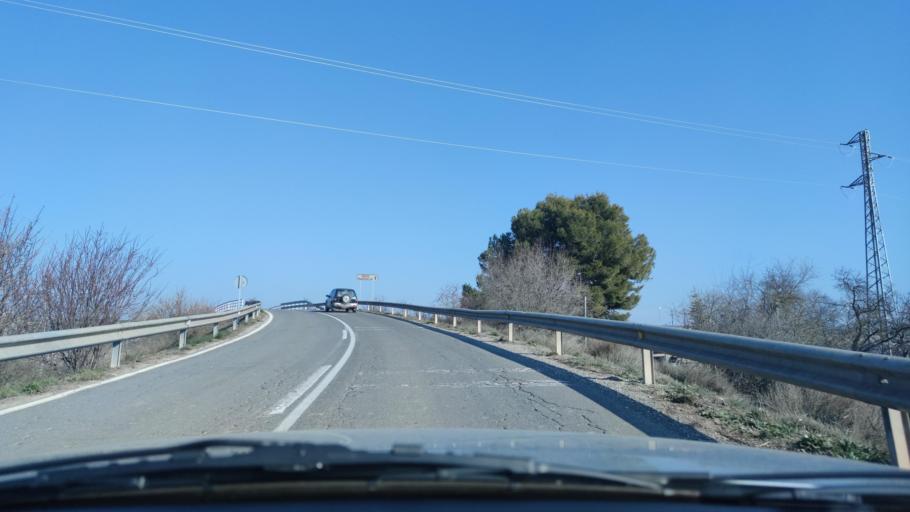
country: ES
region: Catalonia
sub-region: Provincia de Lleida
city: Juneda
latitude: 41.5528
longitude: 0.7380
